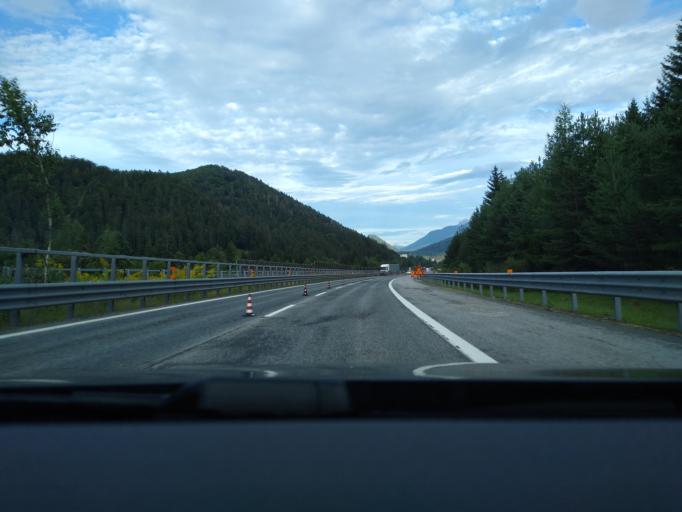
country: IT
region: Friuli Venezia Giulia
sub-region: Provincia di Udine
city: Tarvisio
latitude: 46.5092
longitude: 13.5520
